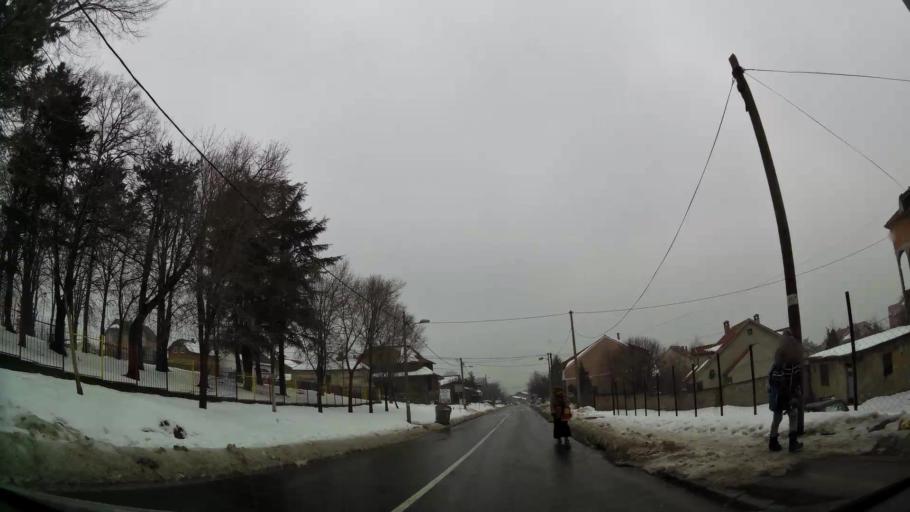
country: RS
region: Central Serbia
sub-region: Belgrade
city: Zvezdara
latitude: 44.7390
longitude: 20.5047
